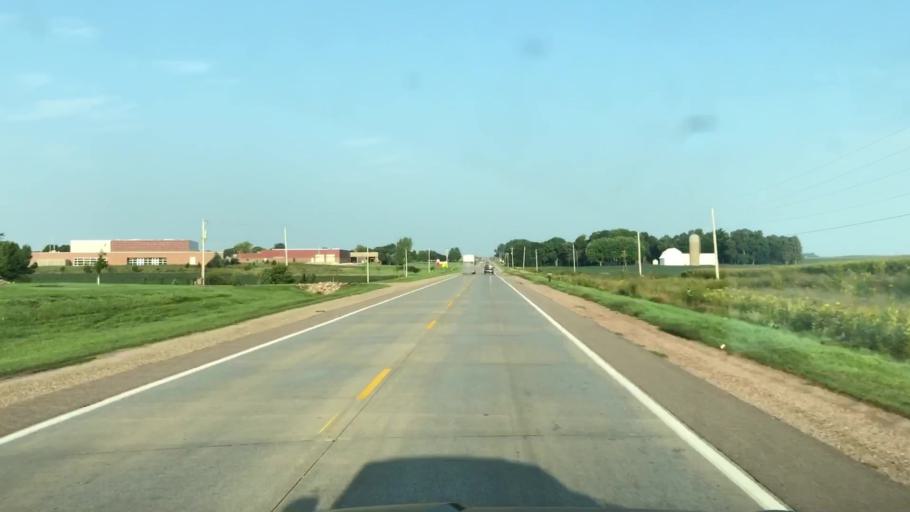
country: US
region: Iowa
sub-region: O'Brien County
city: Sheldon
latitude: 43.1859
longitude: -95.8715
